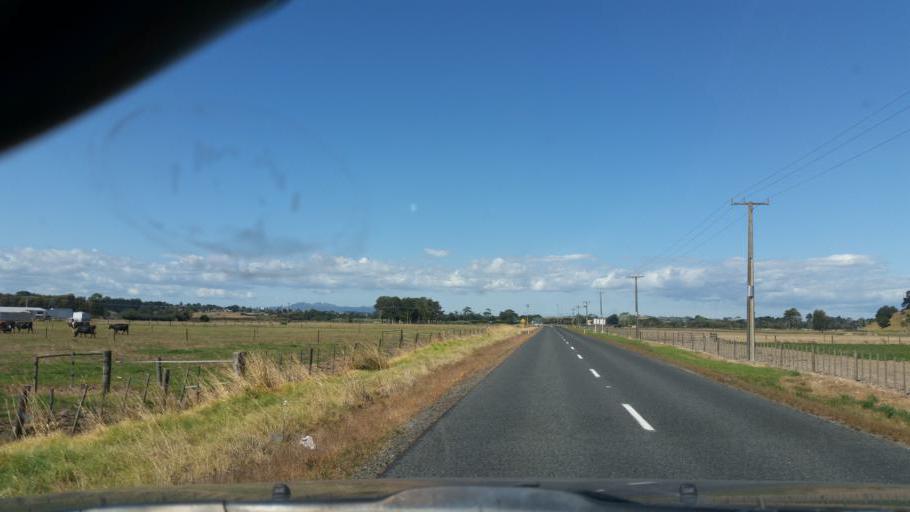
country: NZ
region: Northland
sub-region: Kaipara District
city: Dargaville
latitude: -35.9455
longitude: 173.8391
